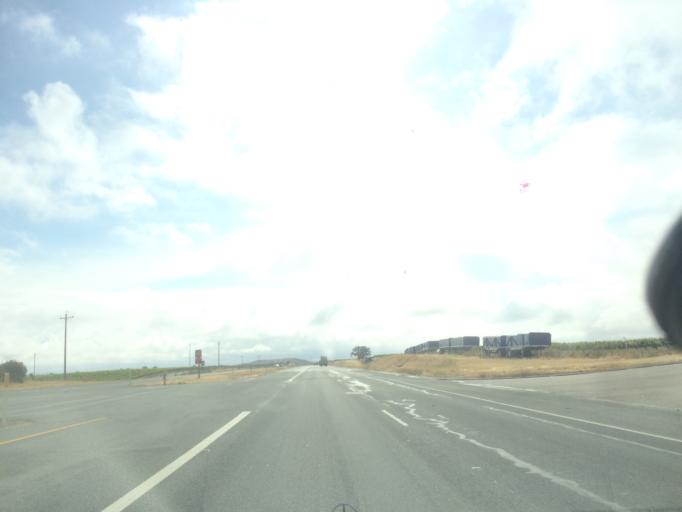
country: US
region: California
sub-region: San Luis Obispo County
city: Paso Robles
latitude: 35.6593
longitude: -120.5703
